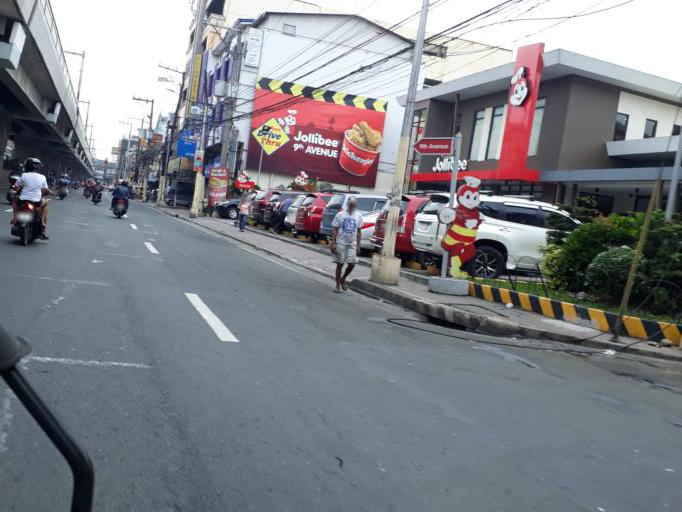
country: PH
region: Metro Manila
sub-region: Caloocan City
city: Niugan
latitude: 14.6501
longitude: 120.9840
